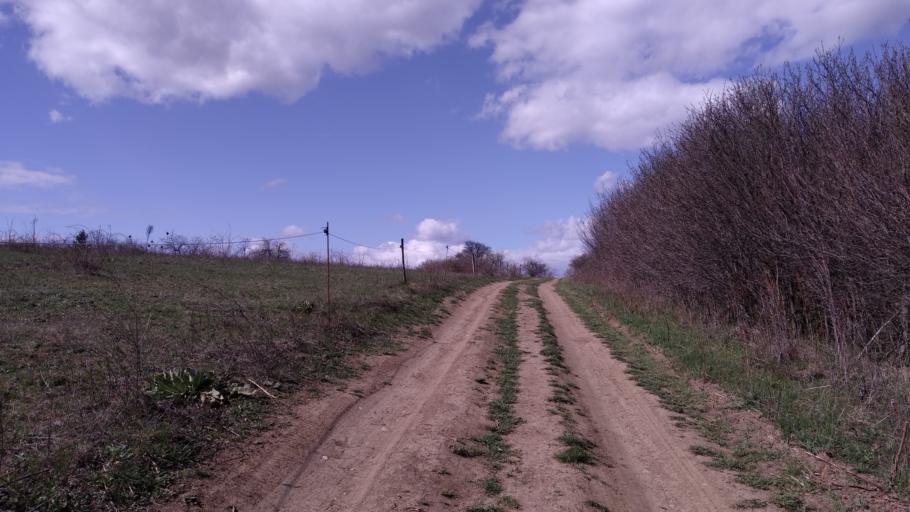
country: HU
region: Pest
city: Pomaz
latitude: 47.6207
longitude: 19.0281
